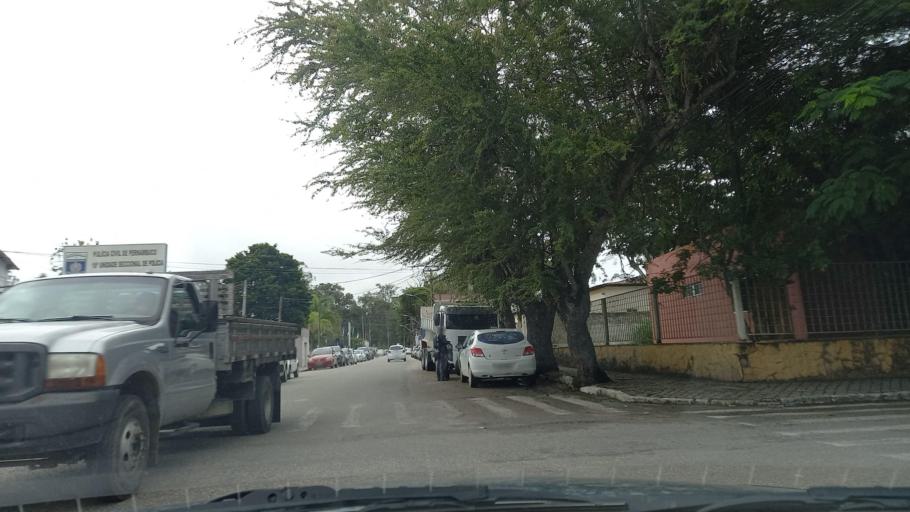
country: BR
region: Pernambuco
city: Garanhuns
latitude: -8.8858
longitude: -36.4879
